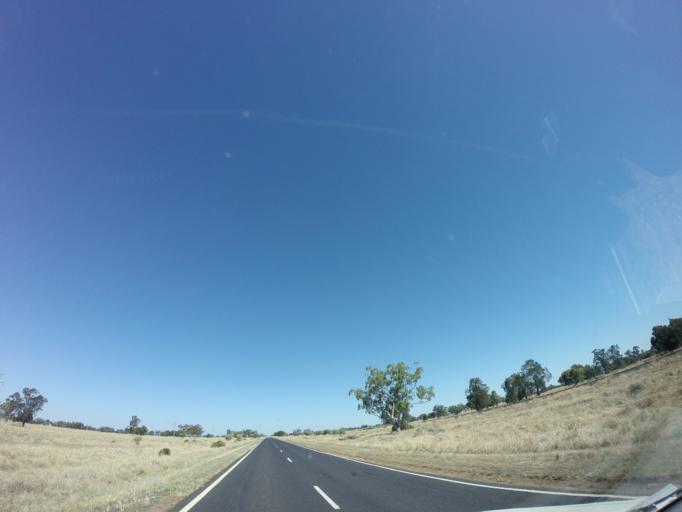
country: AU
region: New South Wales
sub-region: Bogan
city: Nyngan
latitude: -31.7035
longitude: 147.4625
